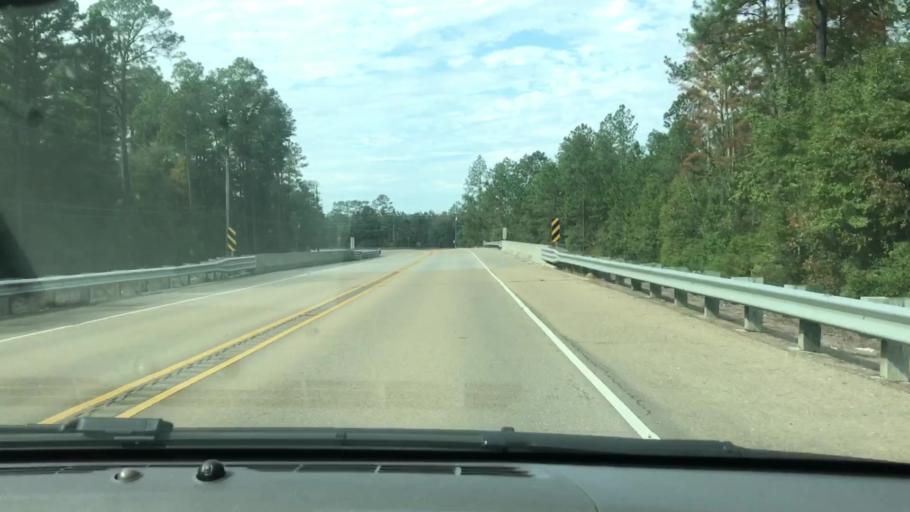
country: US
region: Louisiana
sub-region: Saint Tammany Parish
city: Abita Springs
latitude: 30.5060
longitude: -89.9776
